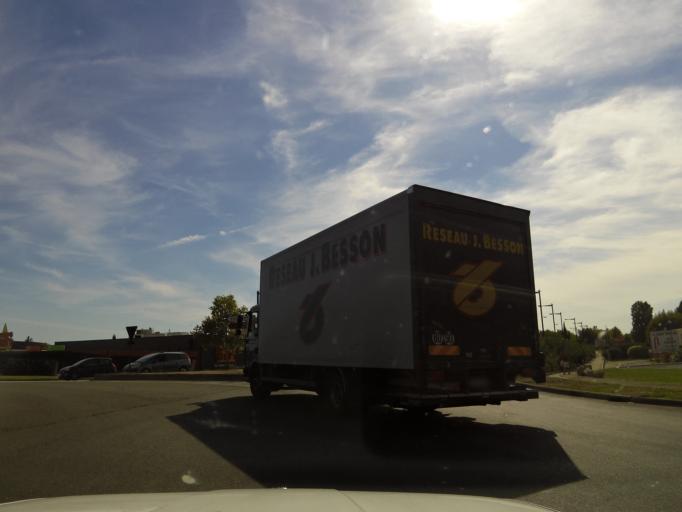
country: FR
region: Languedoc-Roussillon
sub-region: Departement du Gard
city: Nimes
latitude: 43.8179
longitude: 4.3472
